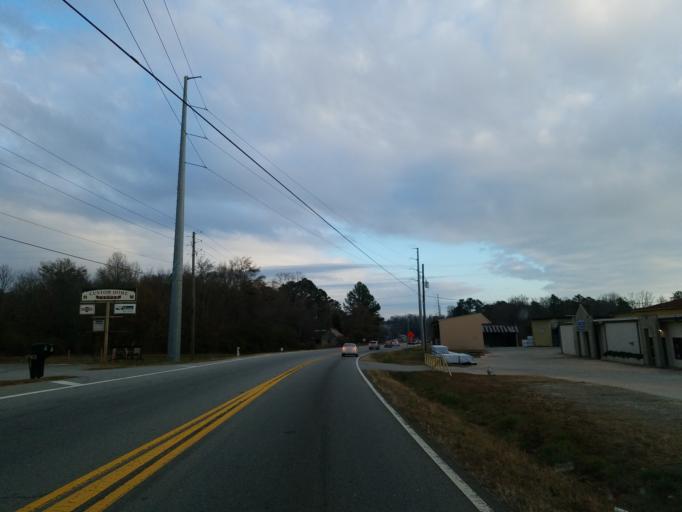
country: US
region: Georgia
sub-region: Forsyth County
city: Cumming
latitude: 34.2699
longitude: -84.0954
